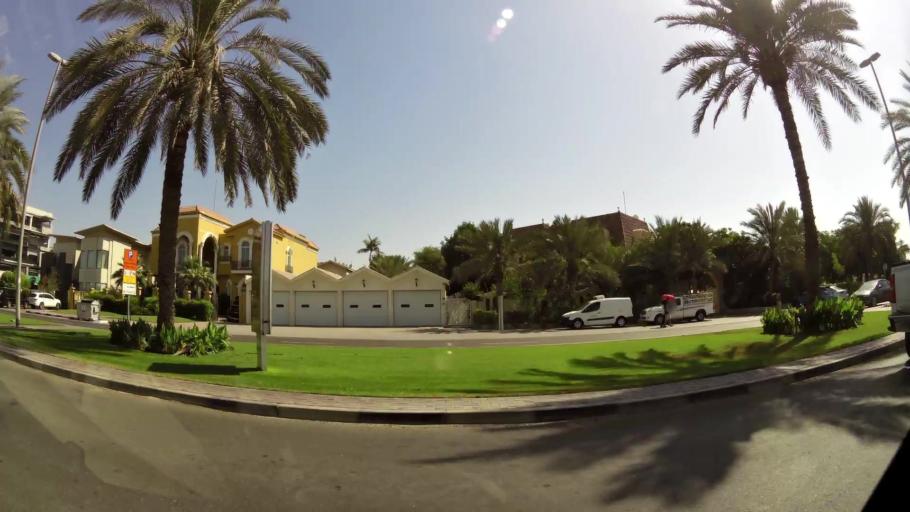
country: AE
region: Ash Shariqah
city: Sharjah
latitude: 25.2424
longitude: 55.2817
